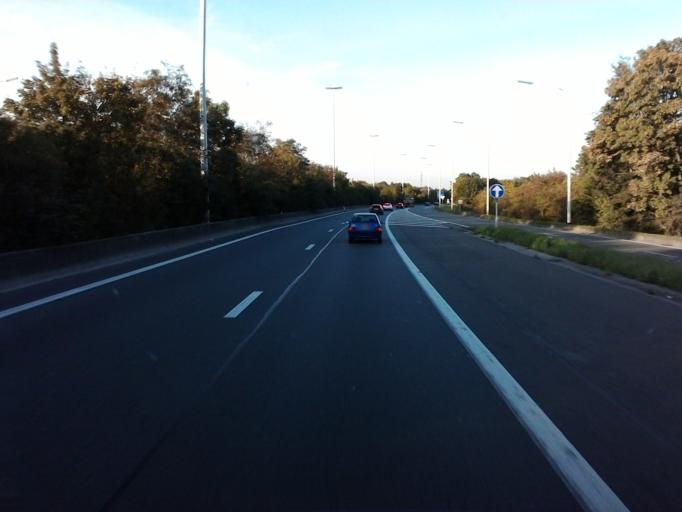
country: BE
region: Wallonia
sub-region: Province de Liege
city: Herstal
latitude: 50.6734
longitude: 5.6485
